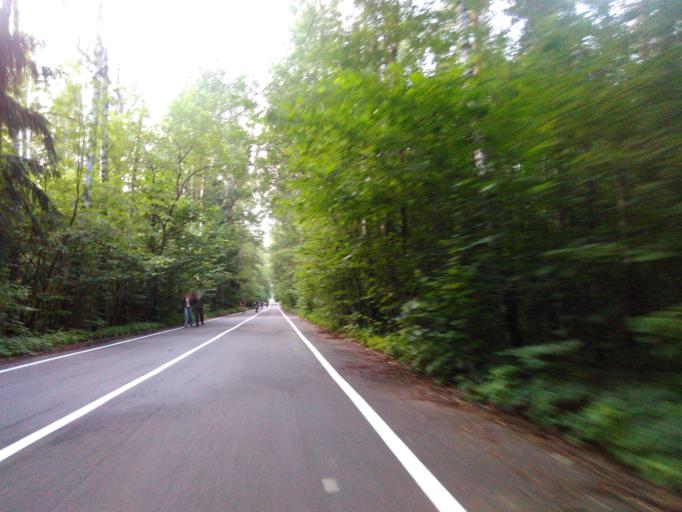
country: RU
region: Moscow
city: Babushkin
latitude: 55.8443
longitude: 37.7265
